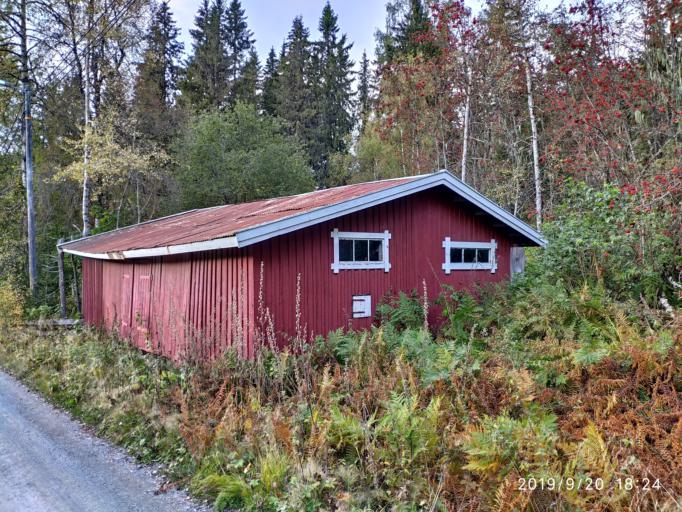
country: NO
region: Buskerud
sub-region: Hole
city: Vik
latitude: 60.0459
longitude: 10.3234
